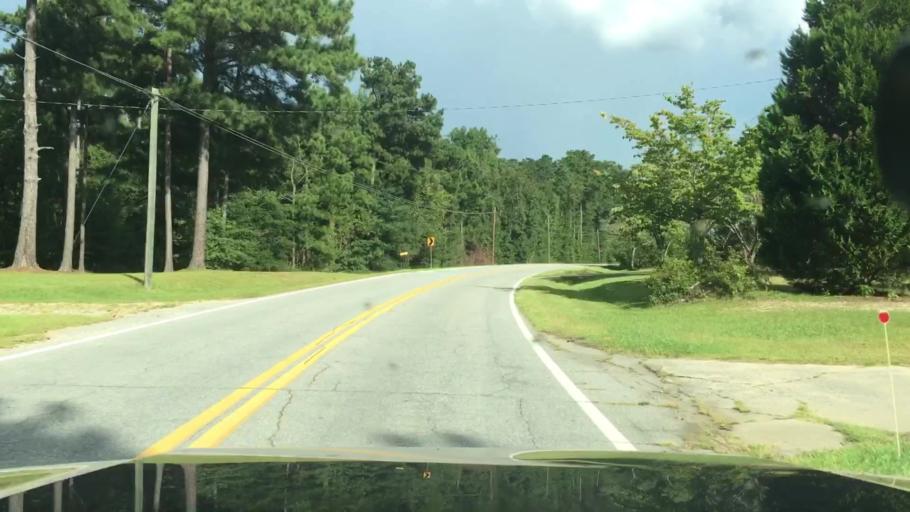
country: US
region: Georgia
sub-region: Bibb County
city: West Point
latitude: 32.8086
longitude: -83.7781
